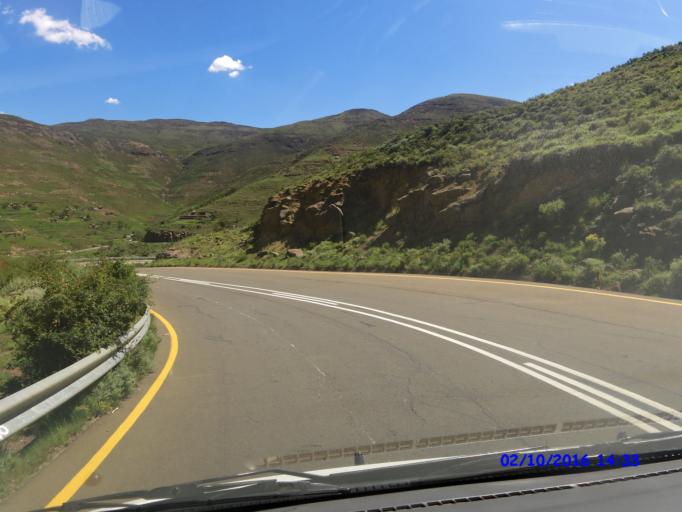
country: LS
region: Maseru
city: Nako
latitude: -29.4886
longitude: 28.0595
